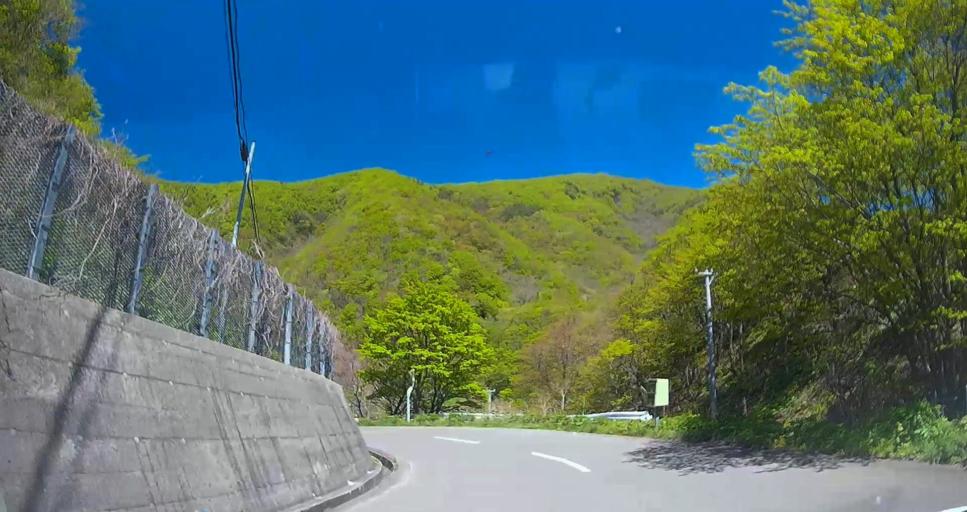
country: JP
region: Aomori
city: Mutsu
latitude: 41.3257
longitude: 140.8138
